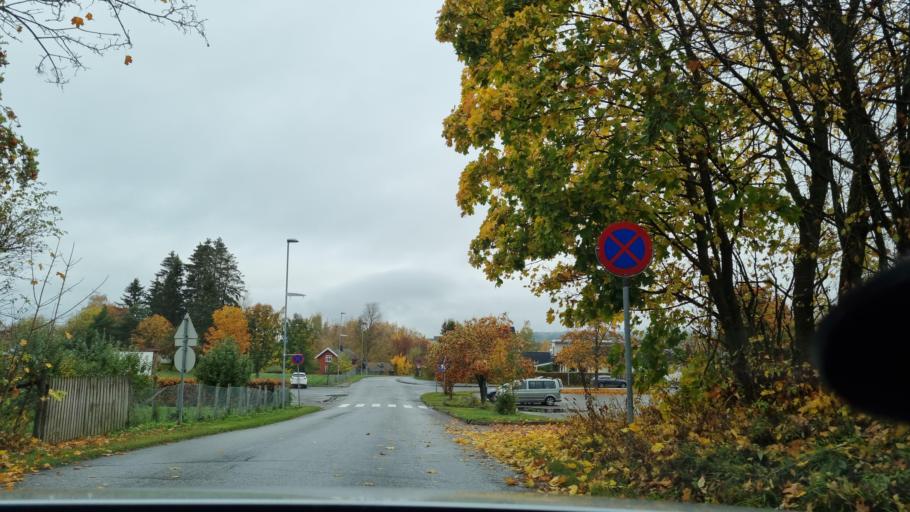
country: NO
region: Hedmark
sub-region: Hamar
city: Hamar
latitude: 60.7929
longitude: 11.0411
